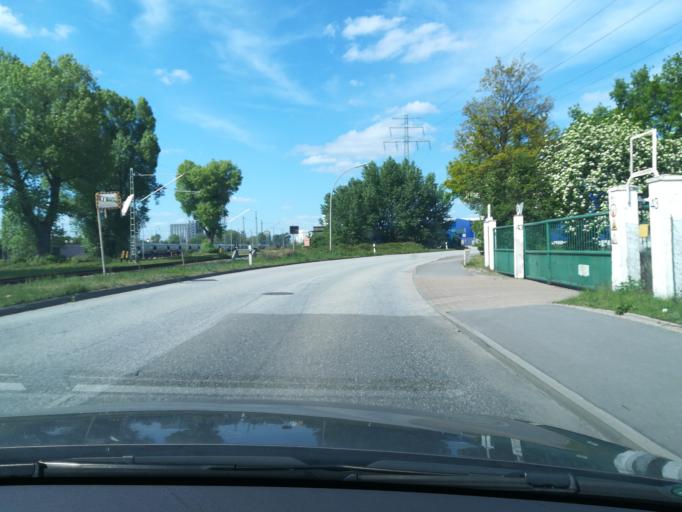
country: DE
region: Hamburg
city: Harburg
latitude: 53.4826
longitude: 9.9791
